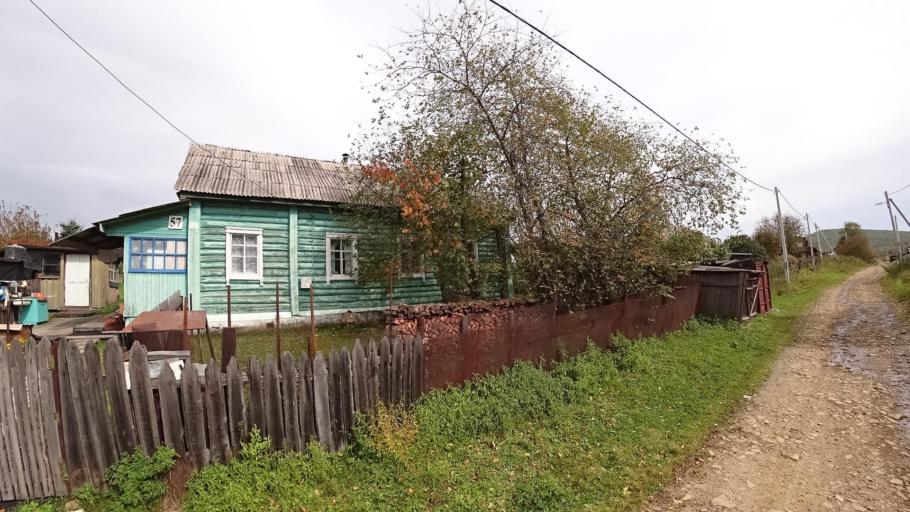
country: RU
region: Jewish Autonomous Oblast
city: Khingansk
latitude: 49.1241
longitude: 131.2060
